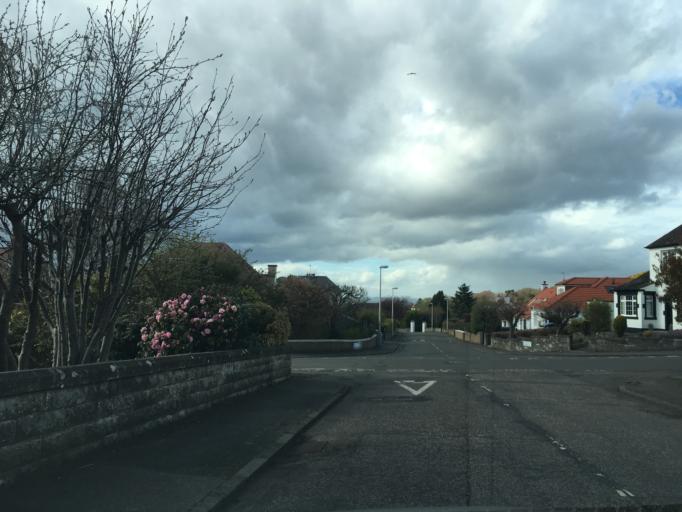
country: GB
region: Scotland
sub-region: Edinburgh
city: Edinburgh
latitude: 55.9066
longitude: -3.2054
